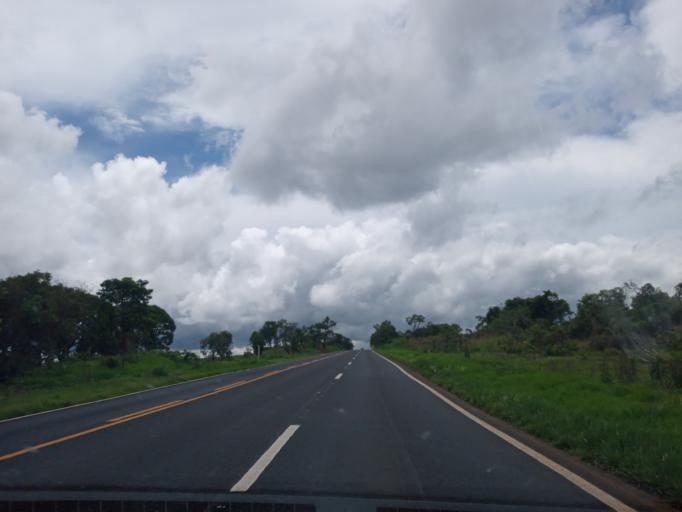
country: BR
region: Minas Gerais
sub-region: Uberaba
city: Uberaba
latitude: -19.2724
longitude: -47.6705
